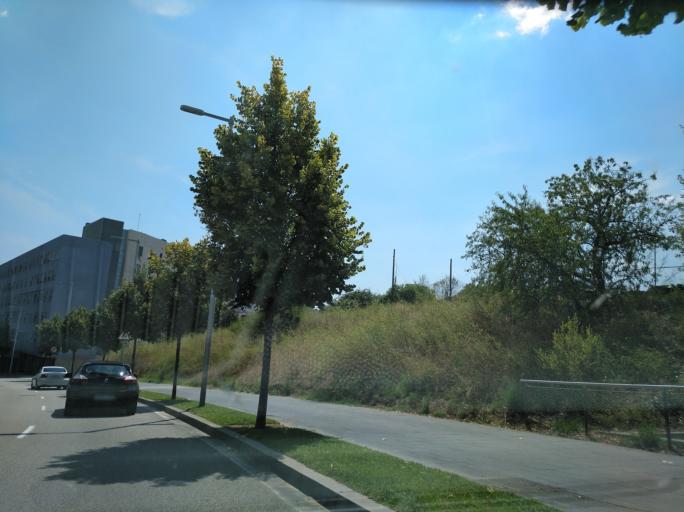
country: ES
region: Catalonia
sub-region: Provincia de Barcelona
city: Horta-Guinardo
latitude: 41.4315
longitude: 2.1539
